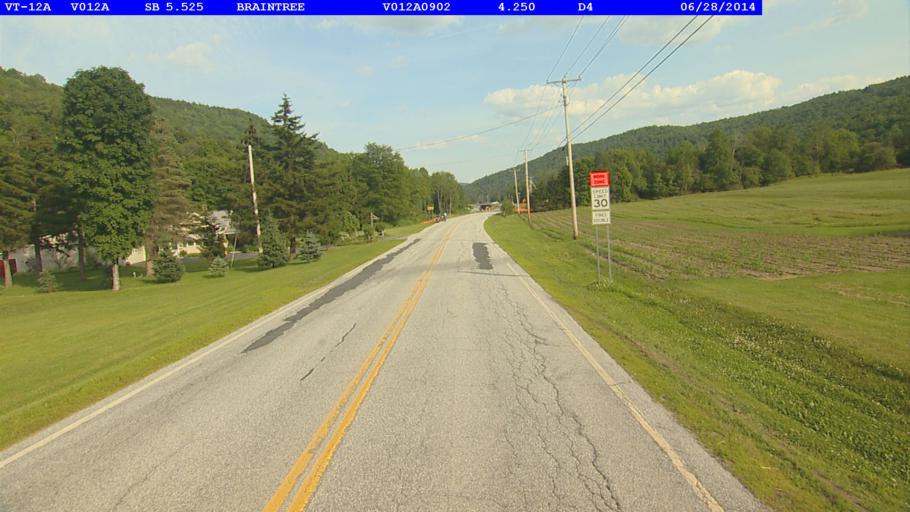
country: US
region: Vermont
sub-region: Orange County
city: Randolph
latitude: 43.9694
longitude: -72.7461
